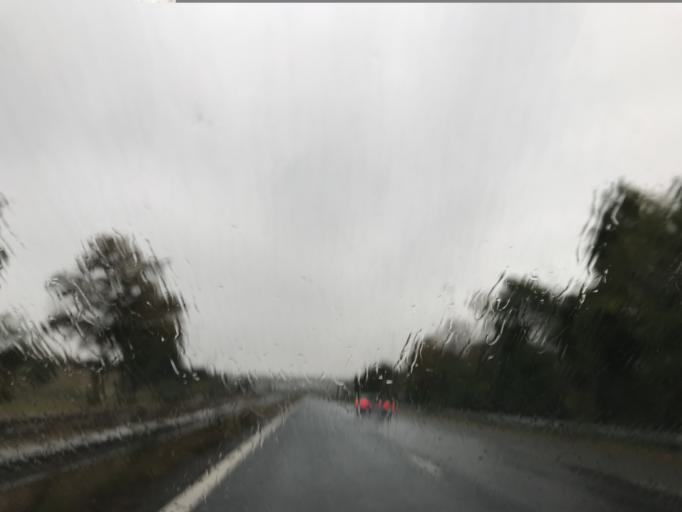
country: FR
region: Auvergne
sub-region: Departement du Puy-de-Dome
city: Aubiere
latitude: 45.7781
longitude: 3.1283
